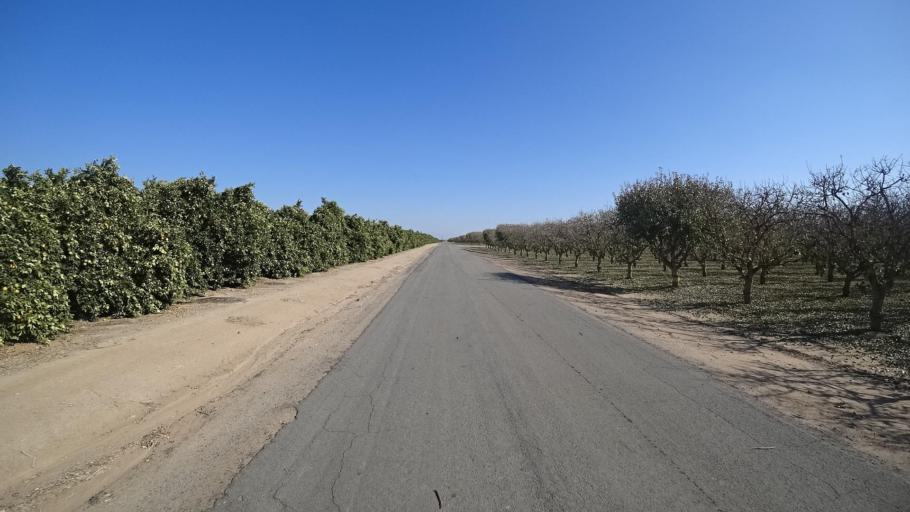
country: US
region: California
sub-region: Kern County
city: McFarland
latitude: 35.6456
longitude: -119.1747
